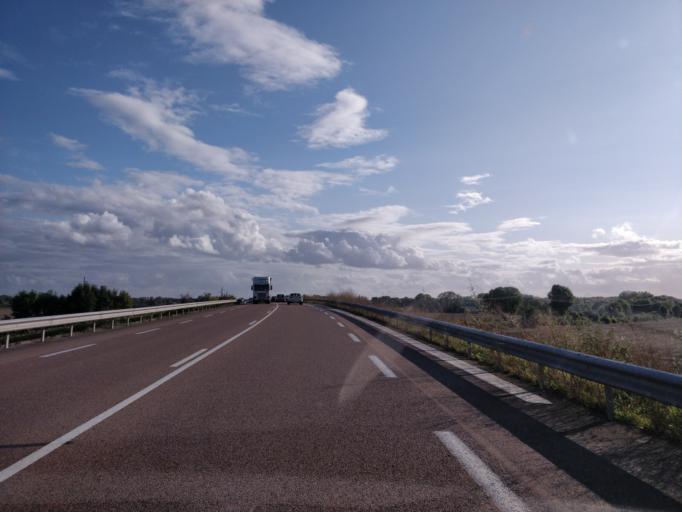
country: FR
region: Champagne-Ardenne
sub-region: Departement de l'Aube
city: Saint-Julien-les-Villas
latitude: 48.2742
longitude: 4.1186
